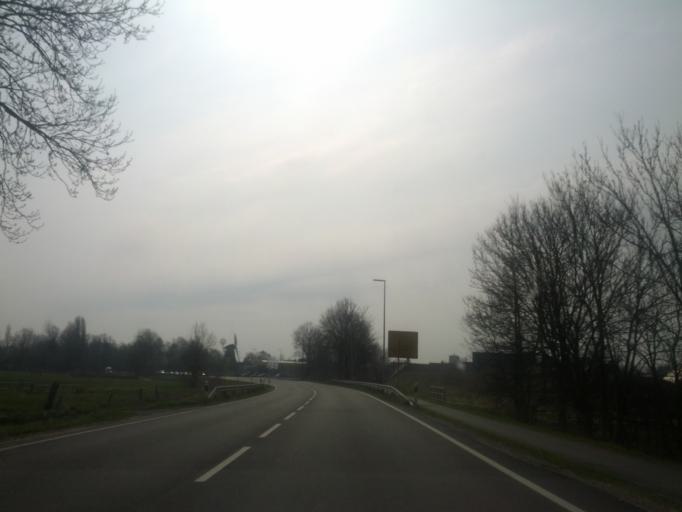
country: DE
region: Lower Saxony
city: Osteel
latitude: 53.5308
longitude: 7.2682
